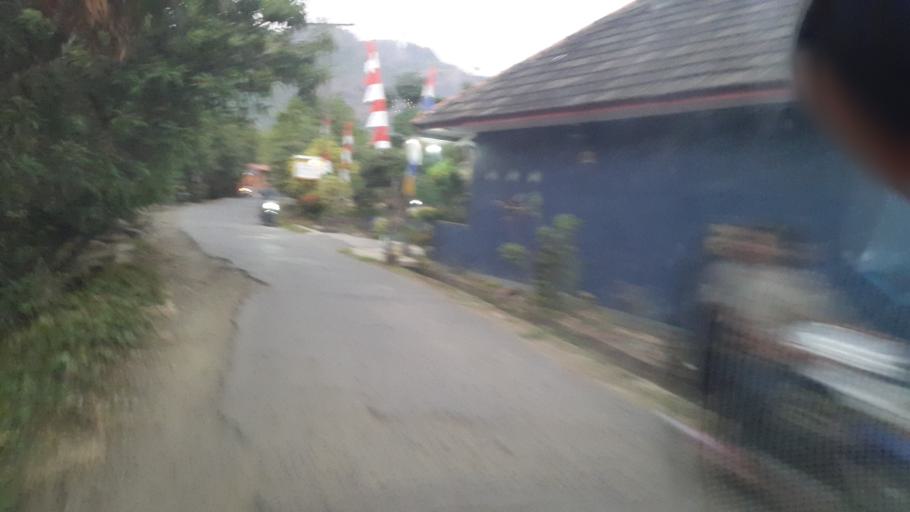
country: ID
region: West Java
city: Ciwaru
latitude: -7.1883
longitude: 106.4871
